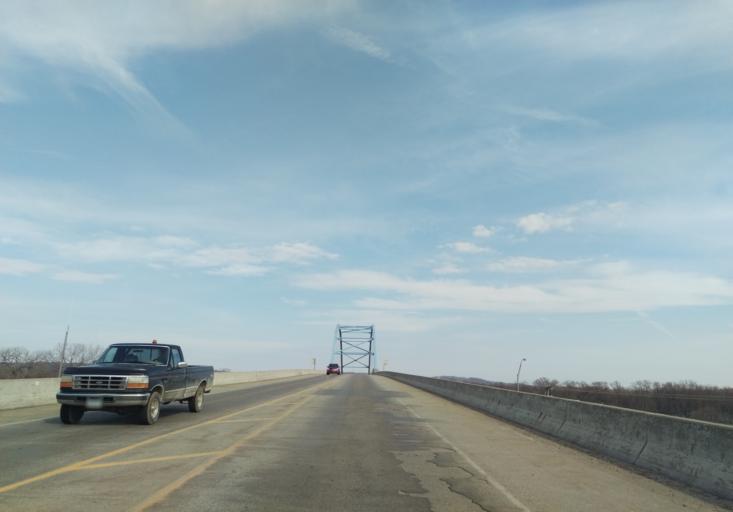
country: US
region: Wisconsin
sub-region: Crawford County
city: Prairie du Chien
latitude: 43.0437
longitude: -91.1793
